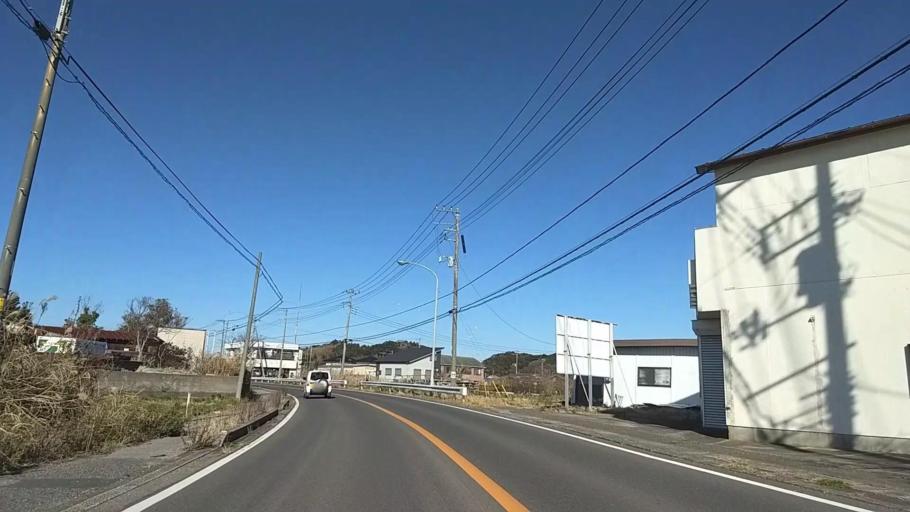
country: JP
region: Chiba
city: Ohara
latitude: 35.3050
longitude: 140.4008
